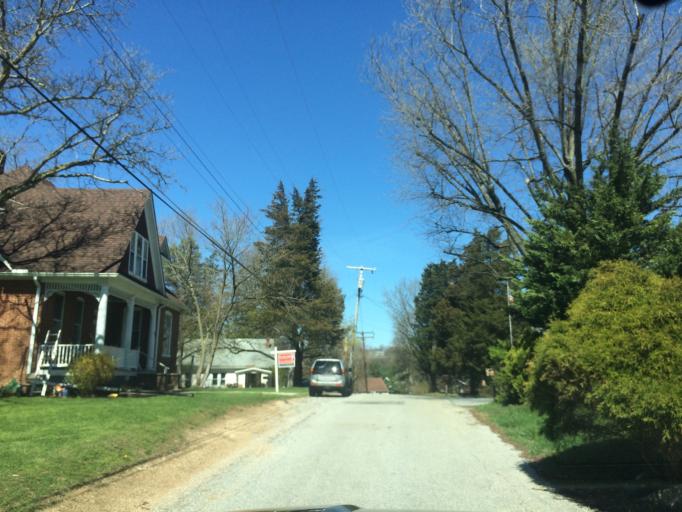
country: US
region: Maryland
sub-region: Carroll County
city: Westminster
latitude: 39.5678
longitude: -77.0005
